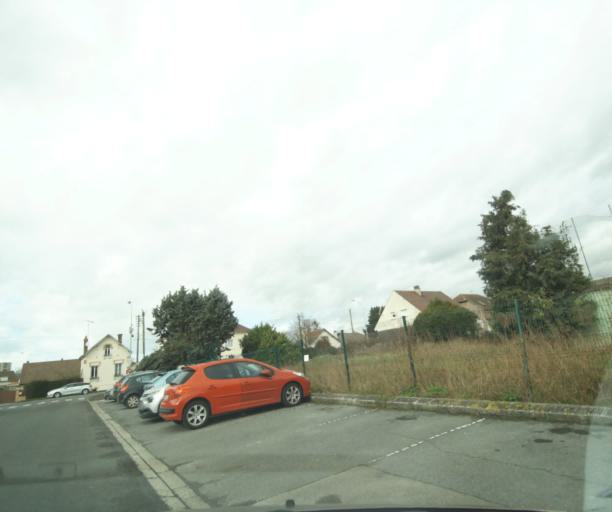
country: FR
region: Picardie
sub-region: Departement de l'Oise
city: Noyon
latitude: 49.5758
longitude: 2.9921
